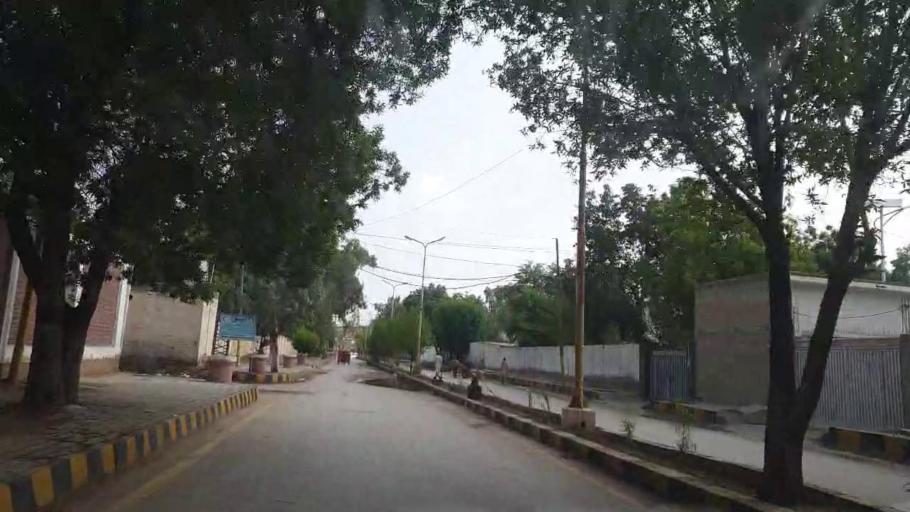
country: PK
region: Sindh
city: Khairpur
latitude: 27.5401
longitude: 68.7560
